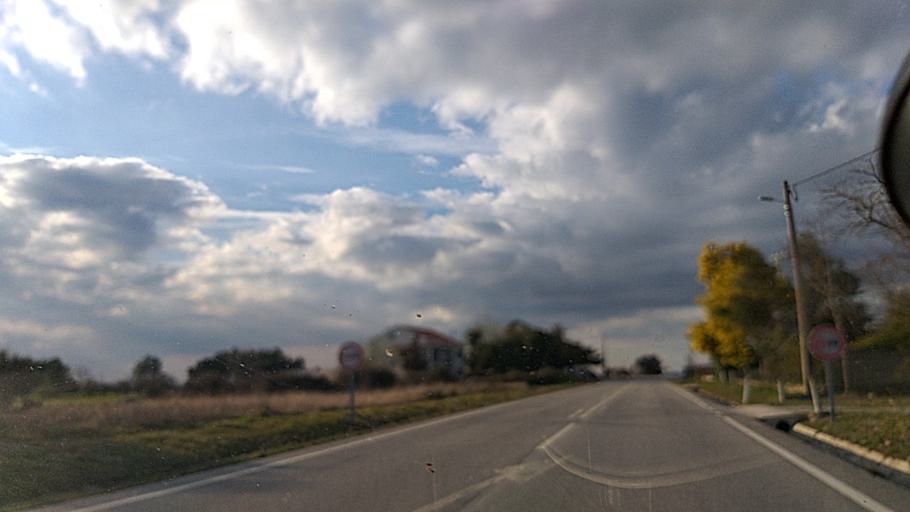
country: ES
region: Castille and Leon
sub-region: Provincia de Salamanca
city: Aldea del Obispo
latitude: 40.7046
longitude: -6.8952
